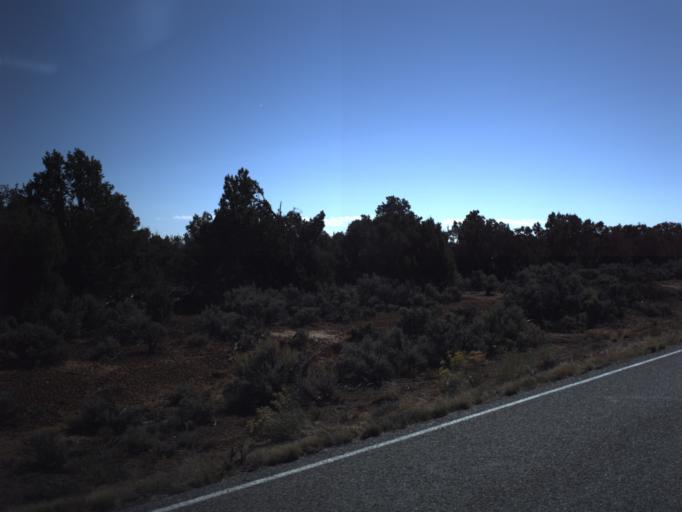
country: US
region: Utah
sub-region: San Juan County
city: Blanding
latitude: 37.3455
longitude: -109.9148
